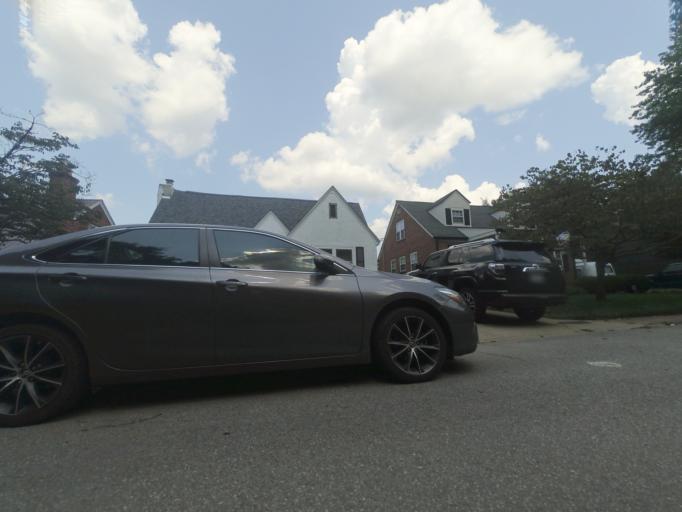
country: US
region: West Virginia
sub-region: Cabell County
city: Huntington
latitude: 38.3960
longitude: -82.4275
